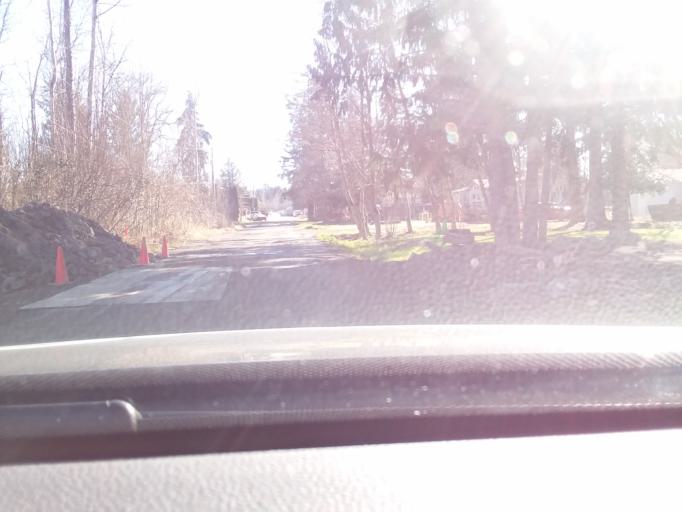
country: US
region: Washington
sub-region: Pierce County
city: Summit
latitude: 47.1365
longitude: -122.3616
